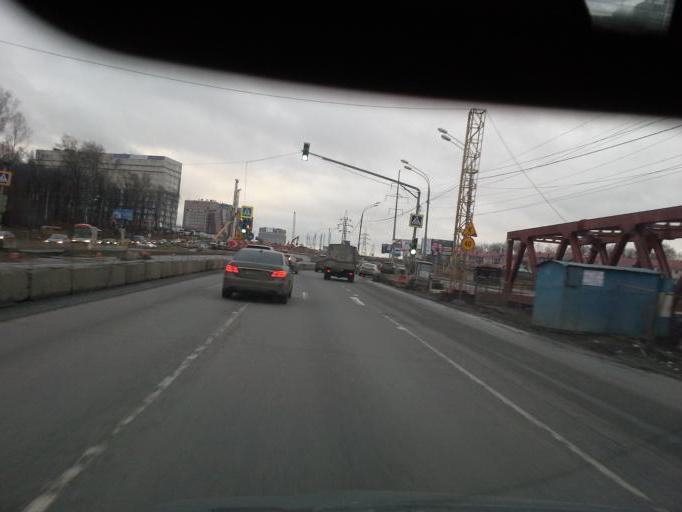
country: RU
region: Moskovskaya
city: Kommunarka
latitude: 55.5888
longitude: 37.4744
